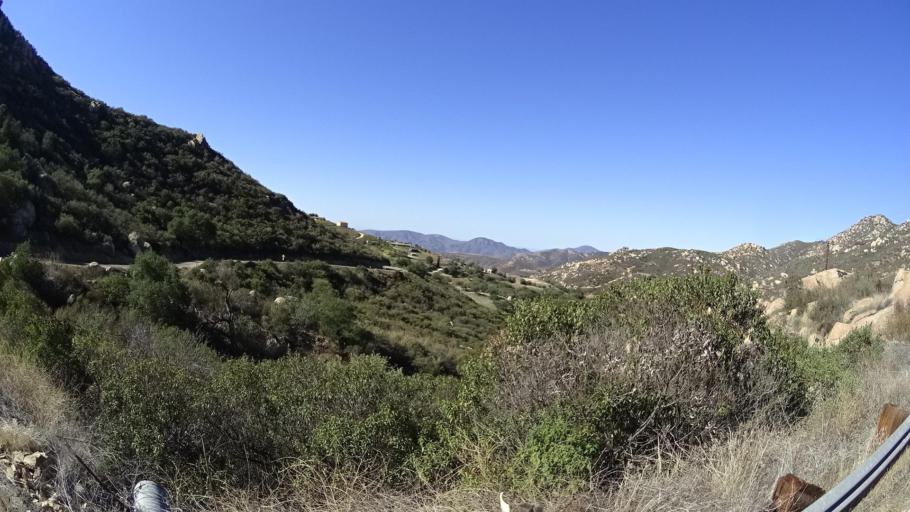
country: US
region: California
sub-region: San Diego County
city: Jamul
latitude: 32.7126
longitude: -116.7751
